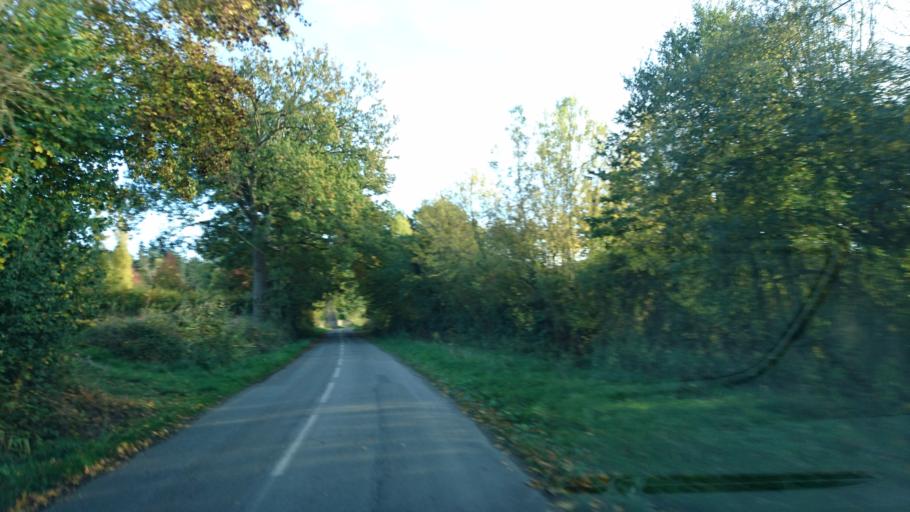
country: FR
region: Brittany
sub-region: Departement d'Ille-et-Vilaine
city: Bruz
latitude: 48.0005
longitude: -1.7537
